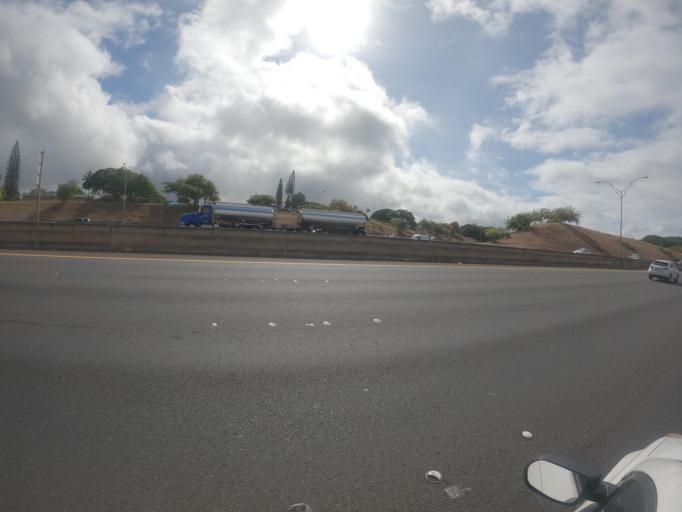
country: US
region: Hawaii
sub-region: Honolulu County
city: Halawa
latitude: 21.3750
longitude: -157.9258
